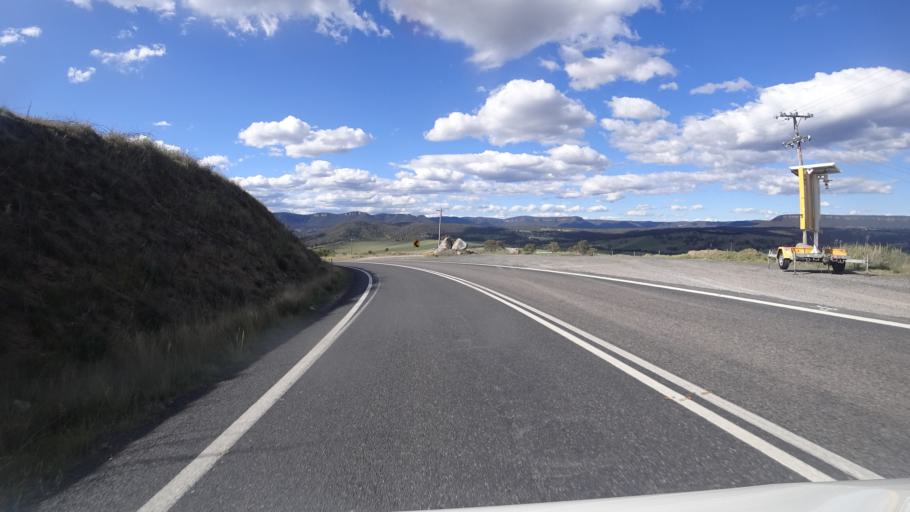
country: AU
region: New South Wales
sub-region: Lithgow
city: Bowenfels
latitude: -33.5658
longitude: 150.1313
